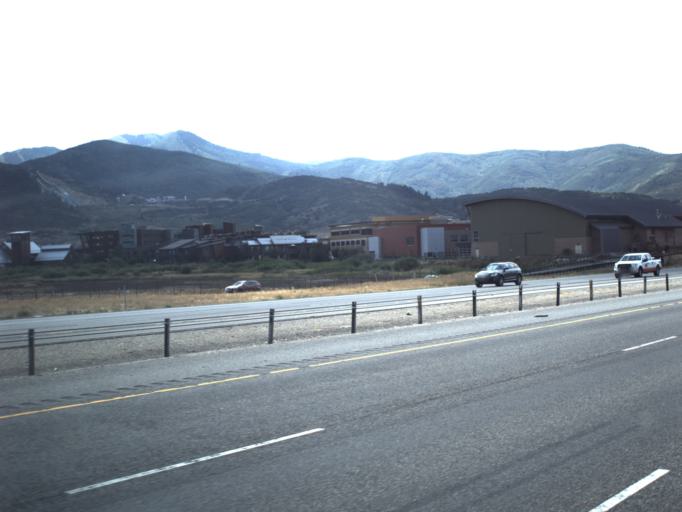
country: US
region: Utah
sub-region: Summit County
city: Snyderville
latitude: 40.7242
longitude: -111.5337
